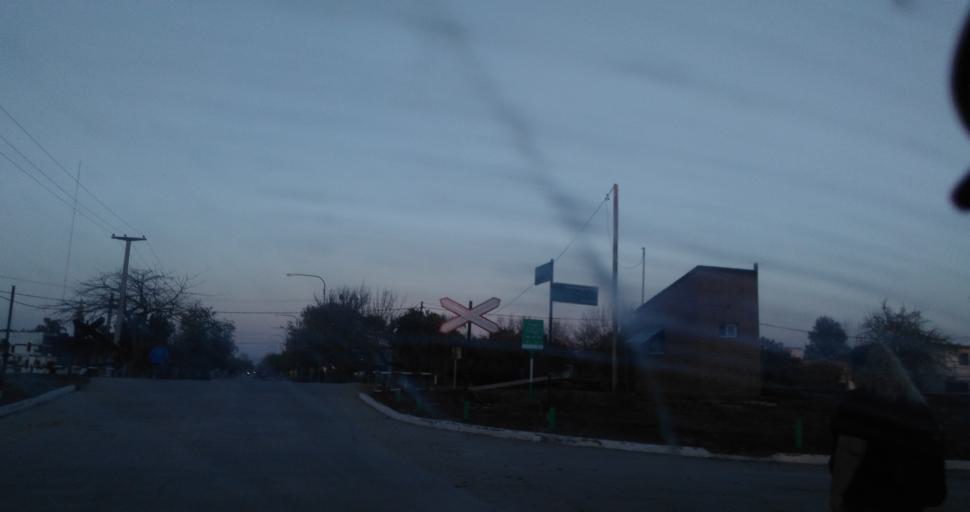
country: AR
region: Chaco
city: Resistencia
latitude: -27.4769
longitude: -58.9658
